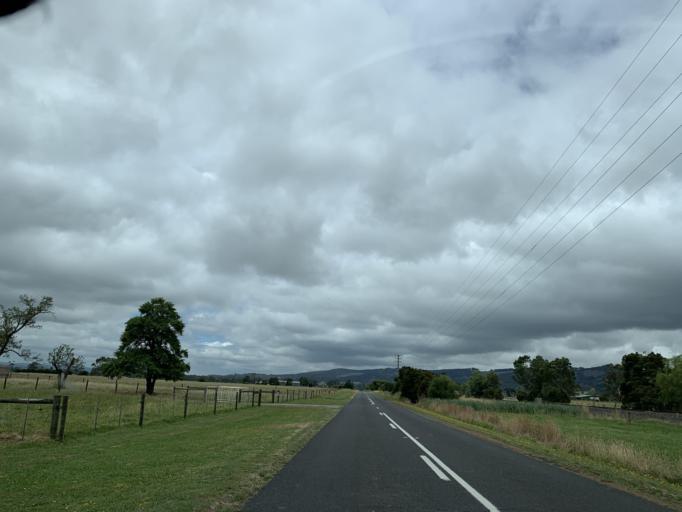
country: AU
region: Victoria
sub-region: Latrobe
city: Moe
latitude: -38.2079
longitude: 146.1248
